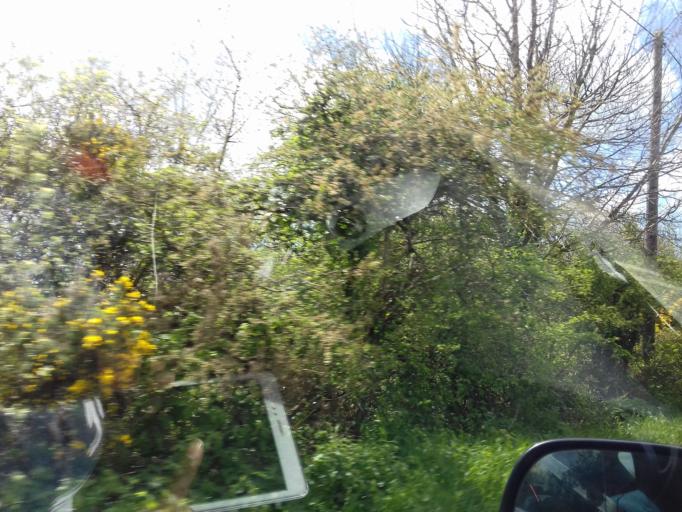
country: IE
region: Leinster
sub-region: Loch Garman
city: Loch Garman
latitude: 52.2868
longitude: -6.6227
